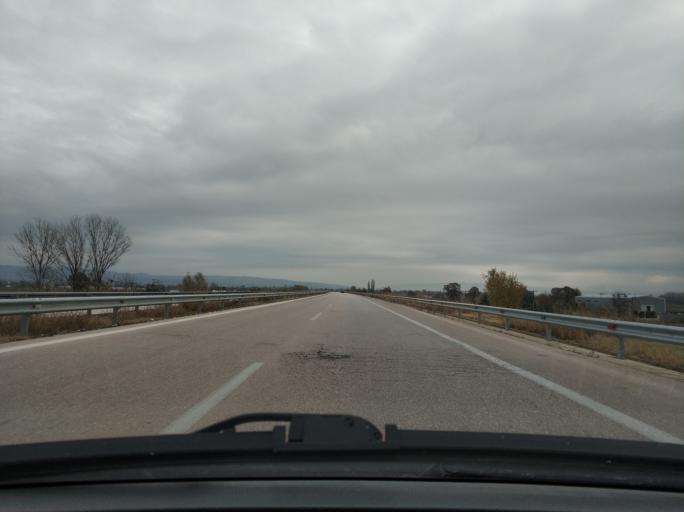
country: GR
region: Central Macedonia
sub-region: Nomos Thessalonikis
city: Lagkadas
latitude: 40.7266
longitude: 23.0744
